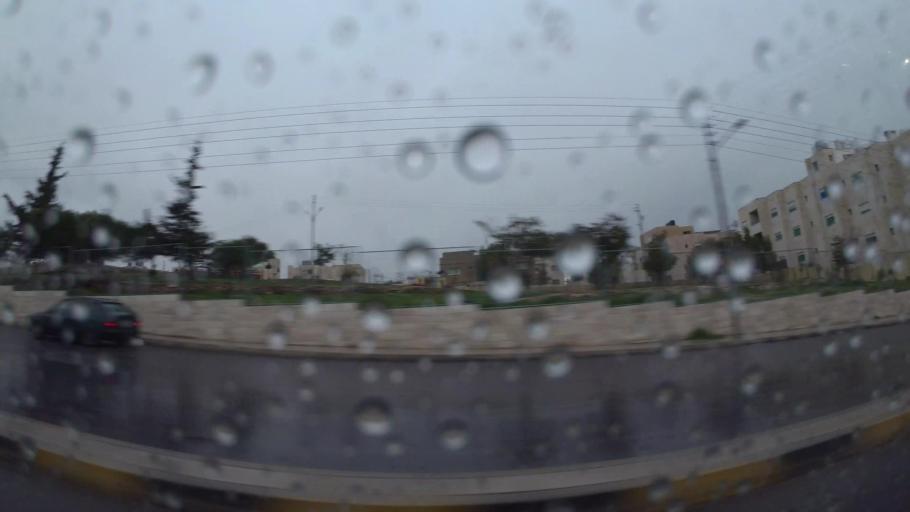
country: JO
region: Amman
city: Amman
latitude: 32.0022
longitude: 35.9602
